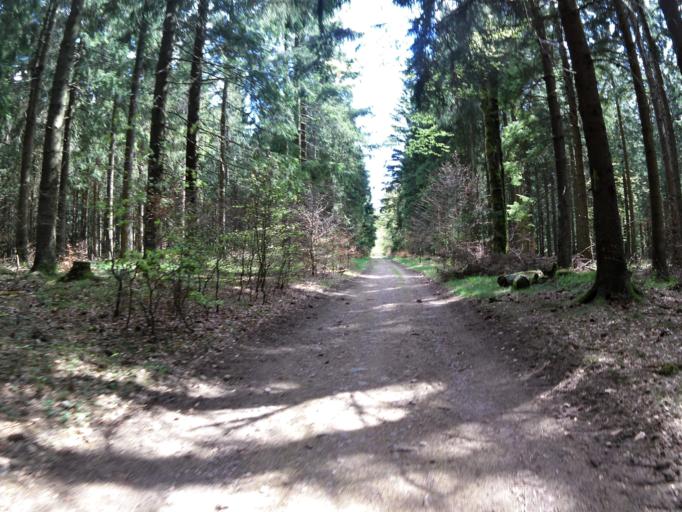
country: DE
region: Thuringia
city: Friedrichroda
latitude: 50.8264
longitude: 10.5383
